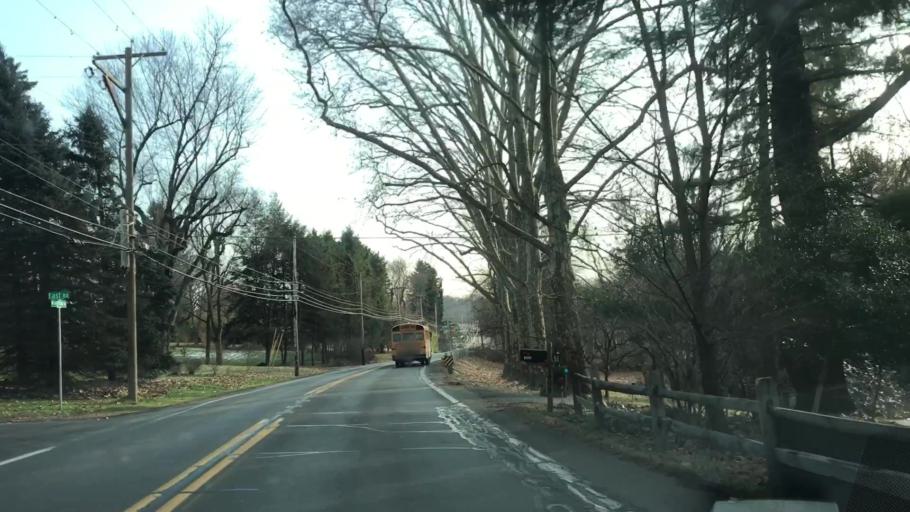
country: US
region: Pennsylvania
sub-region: Allegheny County
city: Franklin Park
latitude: 40.5824
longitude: -80.0611
